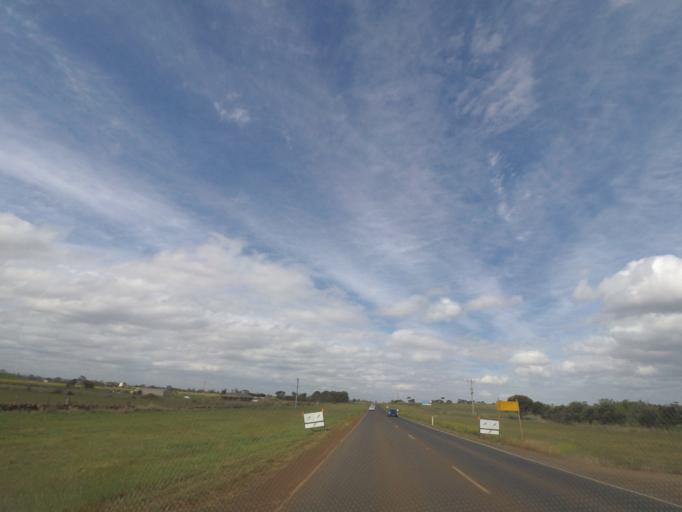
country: AU
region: Victoria
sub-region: Melton
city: Rockbank
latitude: -37.7468
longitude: 144.6848
